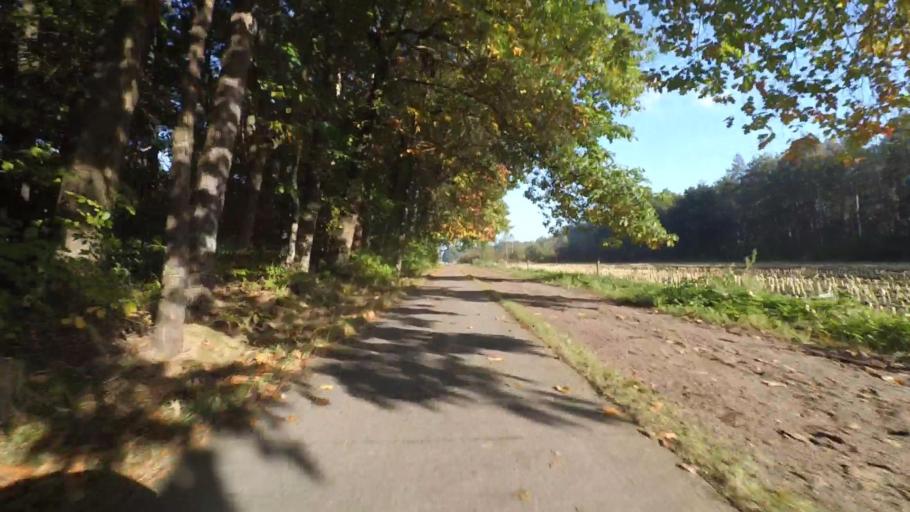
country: NL
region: Gelderland
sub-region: Gemeente Epe
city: Emst
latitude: 52.3138
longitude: 5.9407
